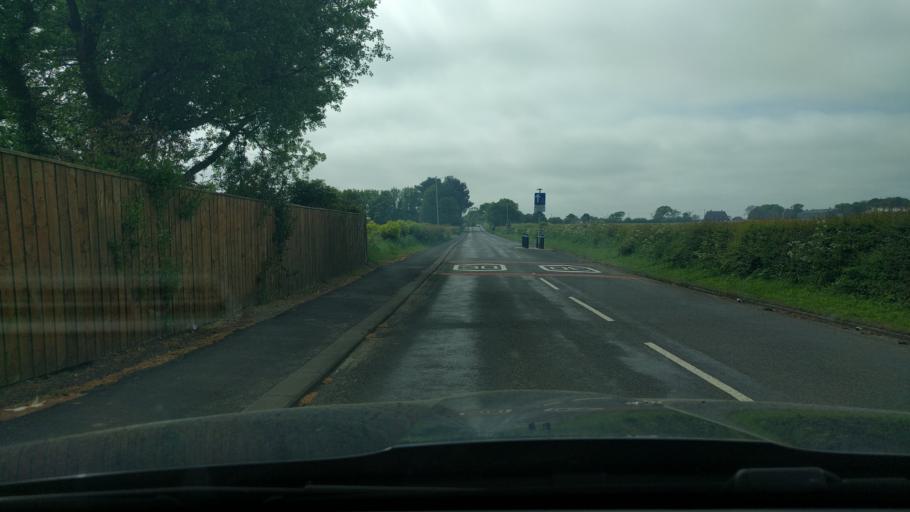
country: GB
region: England
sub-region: Northumberland
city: Acklington
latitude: 55.3016
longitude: -1.6127
